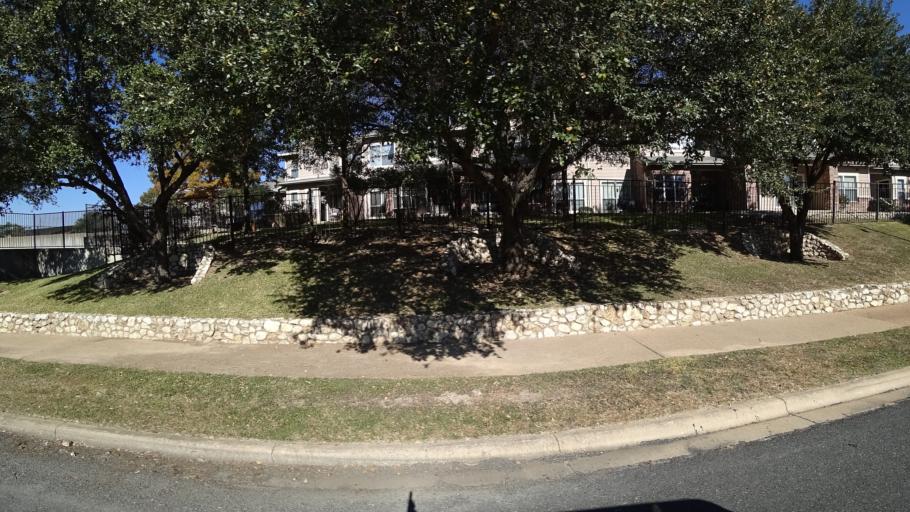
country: US
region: Texas
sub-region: Travis County
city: Wells Branch
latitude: 30.4350
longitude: -97.6961
